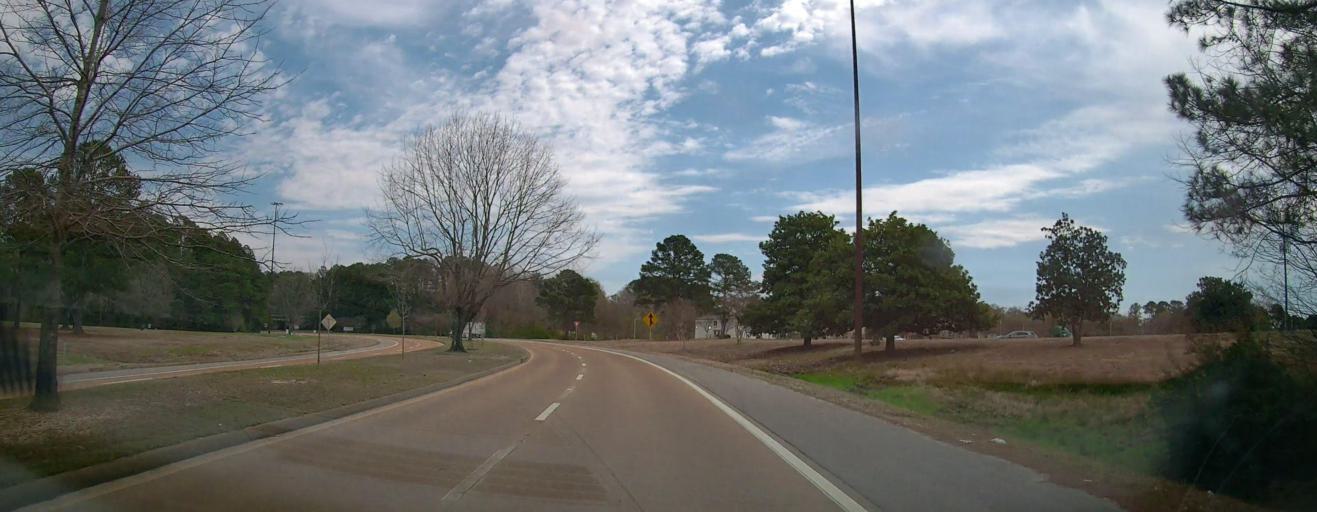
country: US
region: Mississippi
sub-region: Lee County
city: Tupelo
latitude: 34.2730
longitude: -88.7154
